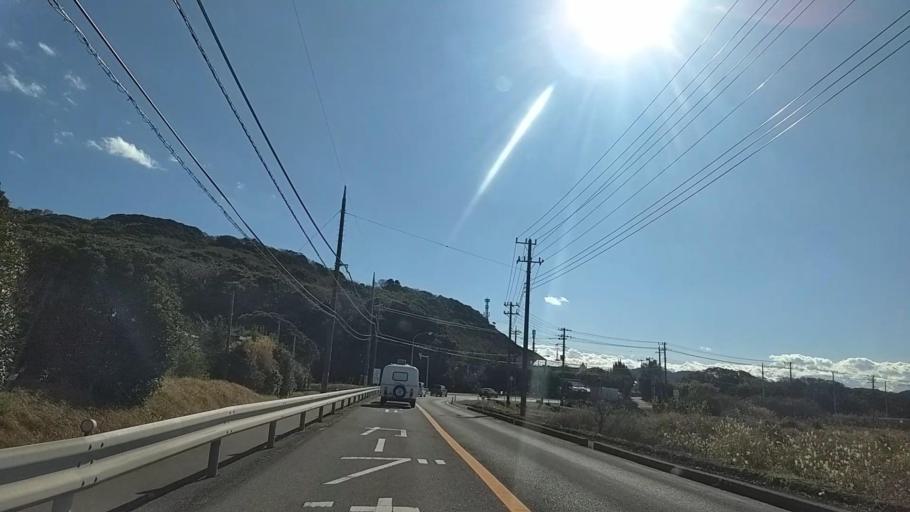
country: JP
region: Chiba
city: Tateyama
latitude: 34.9395
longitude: 139.8413
